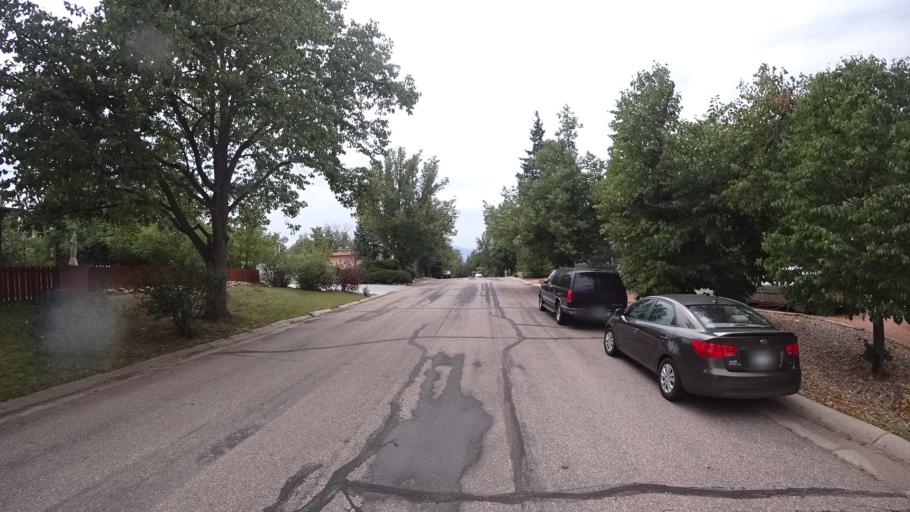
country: US
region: Colorado
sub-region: El Paso County
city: Colorado Springs
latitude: 38.8923
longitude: -104.8090
